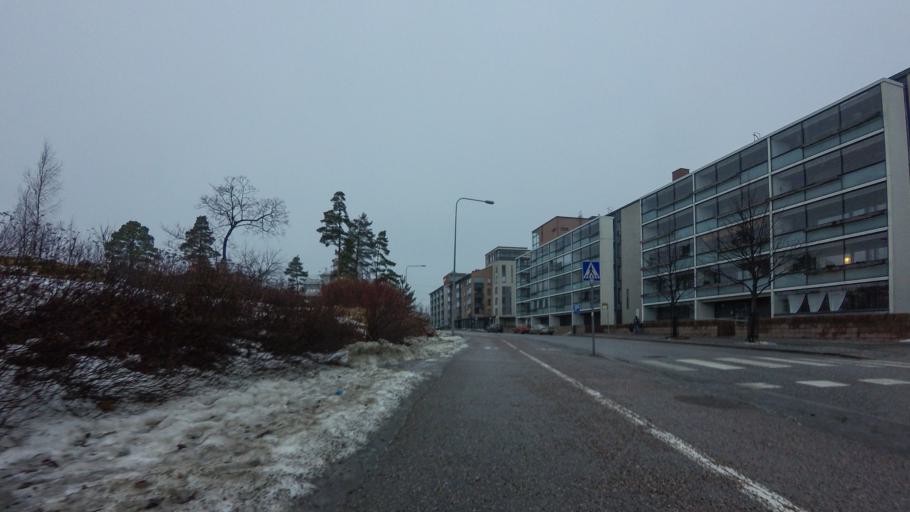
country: FI
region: Uusimaa
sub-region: Helsinki
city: Helsinki
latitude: 60.1902
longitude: 25.0256
